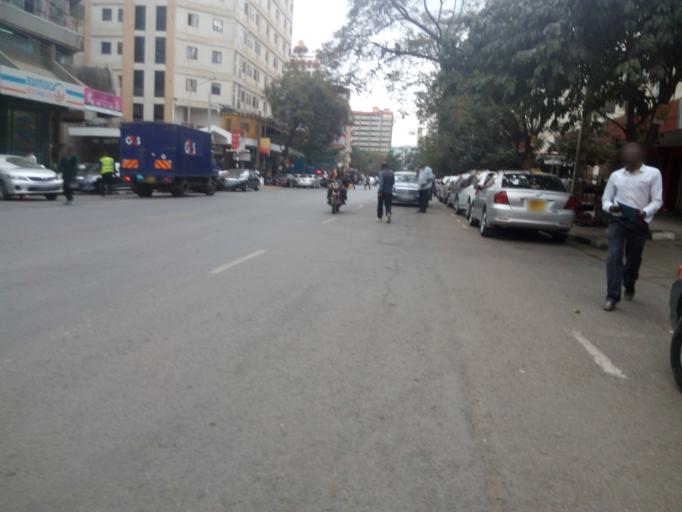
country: KE
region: Nairobi Area
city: Nairobi
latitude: -1.2821
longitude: 36.8179
